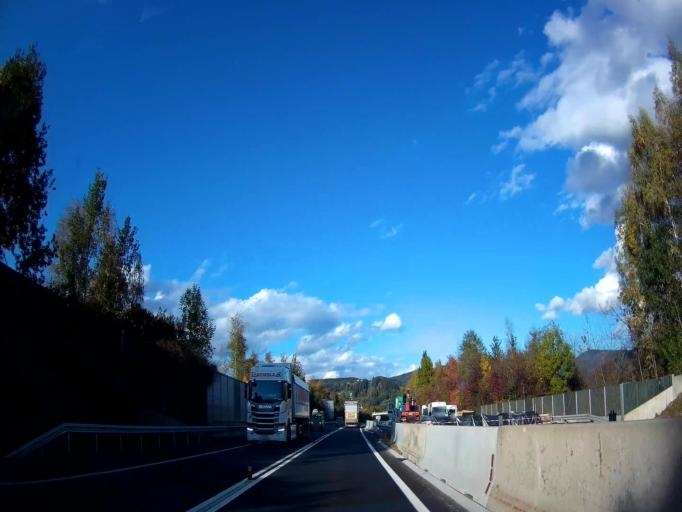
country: AT
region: Carinthia
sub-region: Politischer Bezirk Wolfsberg
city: Wolfsberg
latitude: 46.8326
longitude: 14.8186
